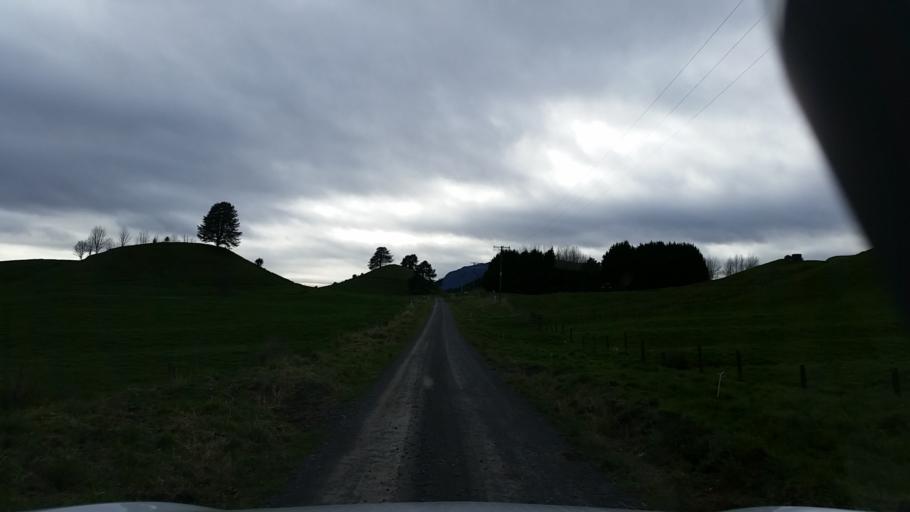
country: NZ
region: Bay of Plenty
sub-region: Rotorua District
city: Rotorua
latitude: -38.3049
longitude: 176.4172
